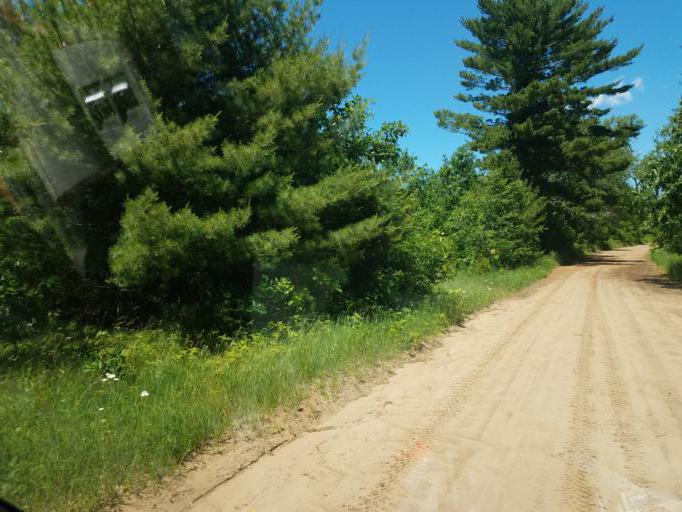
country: US
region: Wisconsin
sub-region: Adams County
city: Friendship
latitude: 44.0270
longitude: -89.9926
